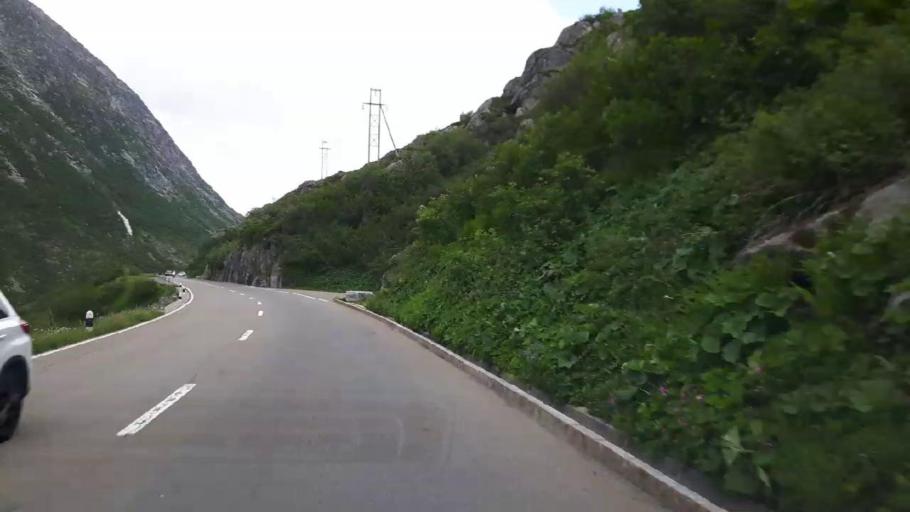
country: CH
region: Uri
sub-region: Uri
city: Andermatt
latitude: 46.5997
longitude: 8.5630
